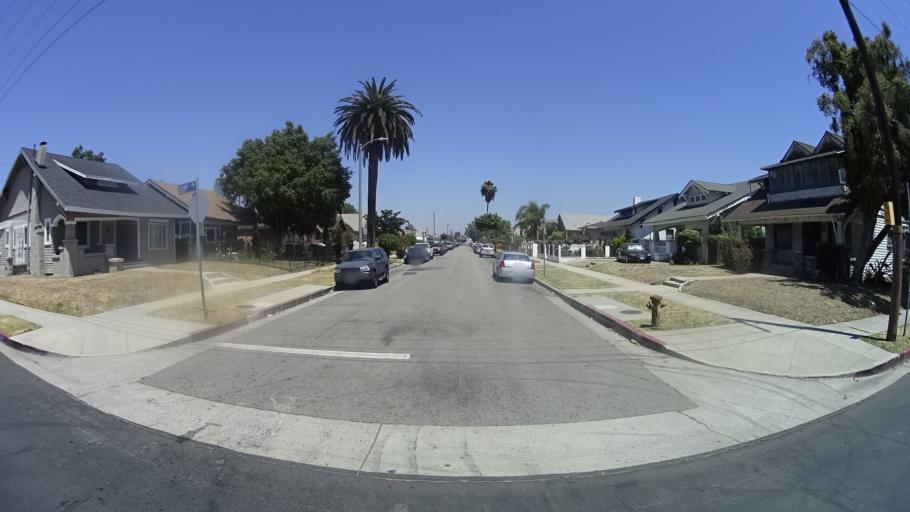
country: US
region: California
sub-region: Los Angeles County
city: View Park-Windsor Hills
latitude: 34.0009
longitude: -118.3045
